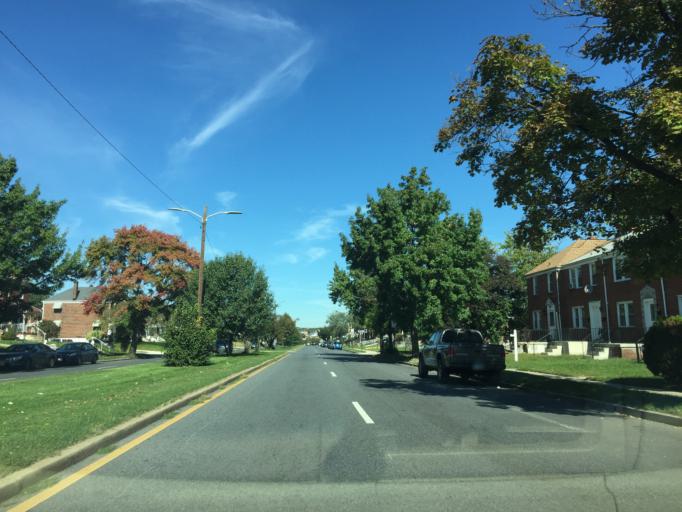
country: US
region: Maryland
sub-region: City of Baltimore
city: Baltimore
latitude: 39.3158
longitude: -76.5689
